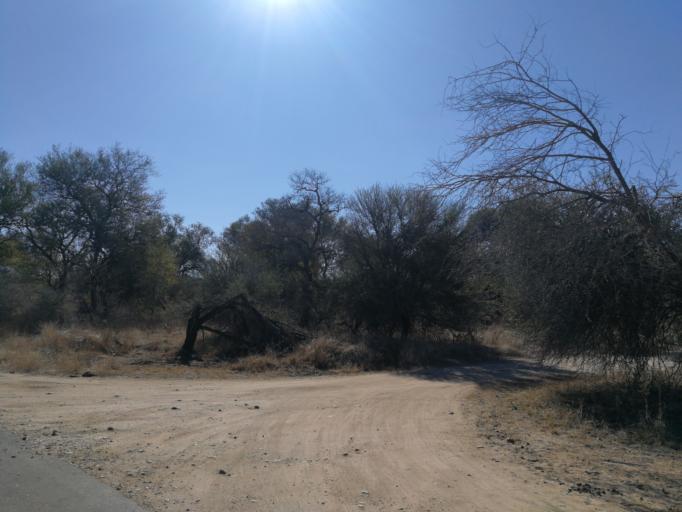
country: ZA
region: Limpopo
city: Thulamahashi
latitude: -24.9661
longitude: 31.6818
